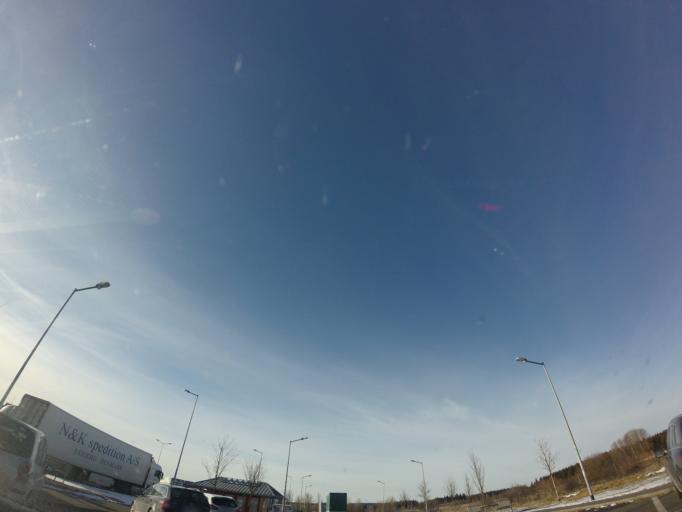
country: DE
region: Bavaria
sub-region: Upper Franconia
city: Leupoldsgrun
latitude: 50.3038
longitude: 11.8064
